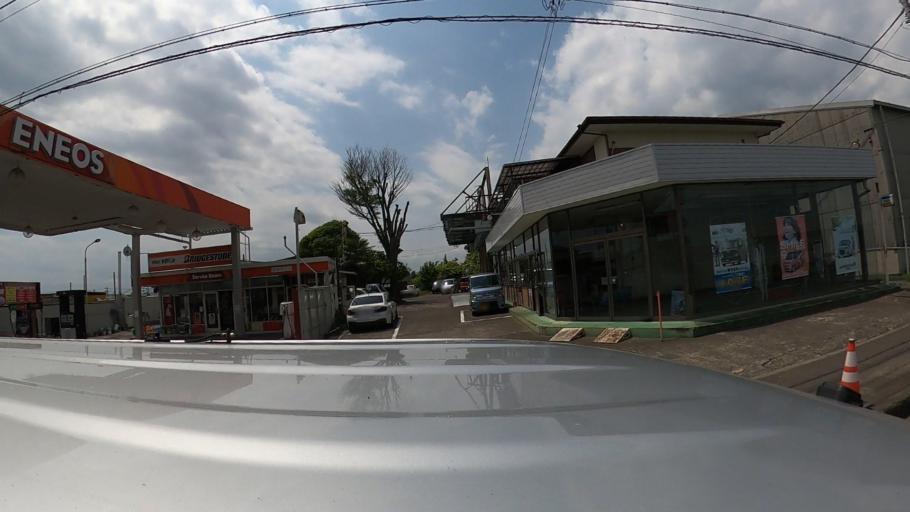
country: JP
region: Kanagawa
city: Chigasaki
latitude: 35.3857
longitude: 139.4018
